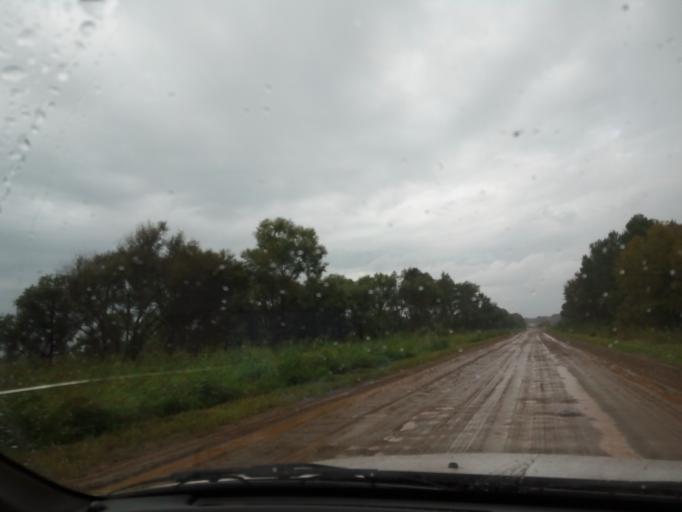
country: RU
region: Primorskiy
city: Lazo
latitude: 45.8476
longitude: 133.6452
